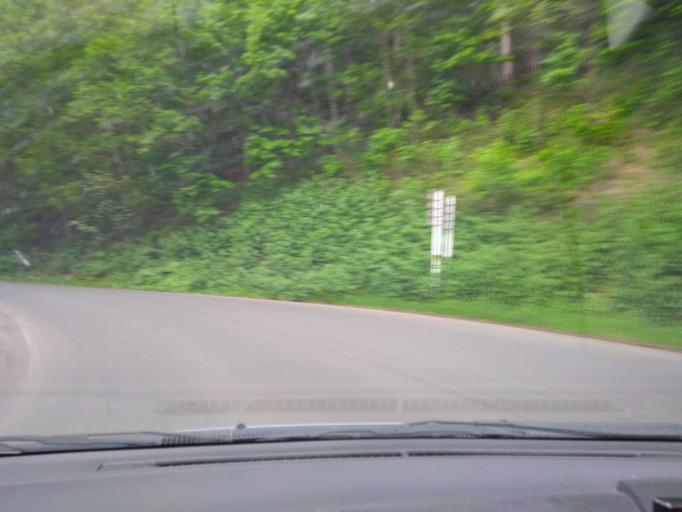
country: JP
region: Hokkaido
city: Shimo-furano
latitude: 43.1391
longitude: 142.4662
